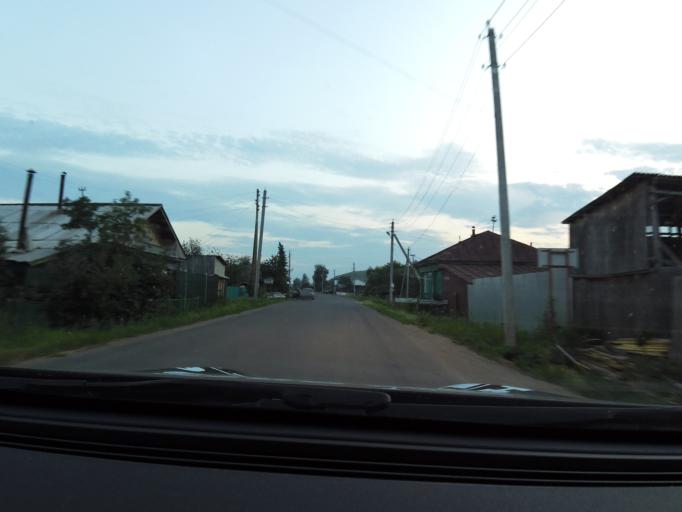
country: RU
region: Sverdlovsk
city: Arti
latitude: 56.1895
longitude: 58.3466
